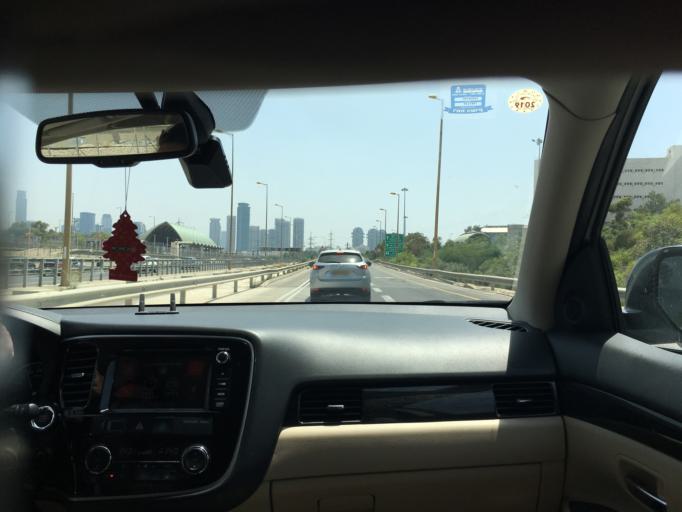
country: IL
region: Tel Aviv
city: Ramat Gan
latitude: 32.1055
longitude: 34.8051
